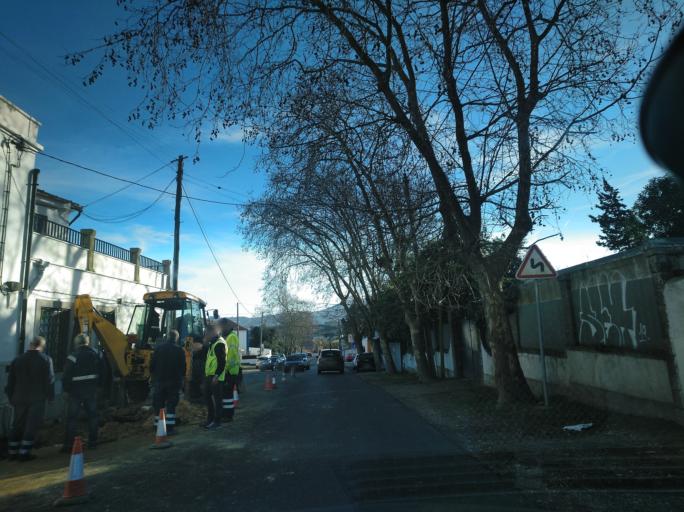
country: PT
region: Lisbon
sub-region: Sintra
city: Sintra
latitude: 38.8341
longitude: -9.3696
